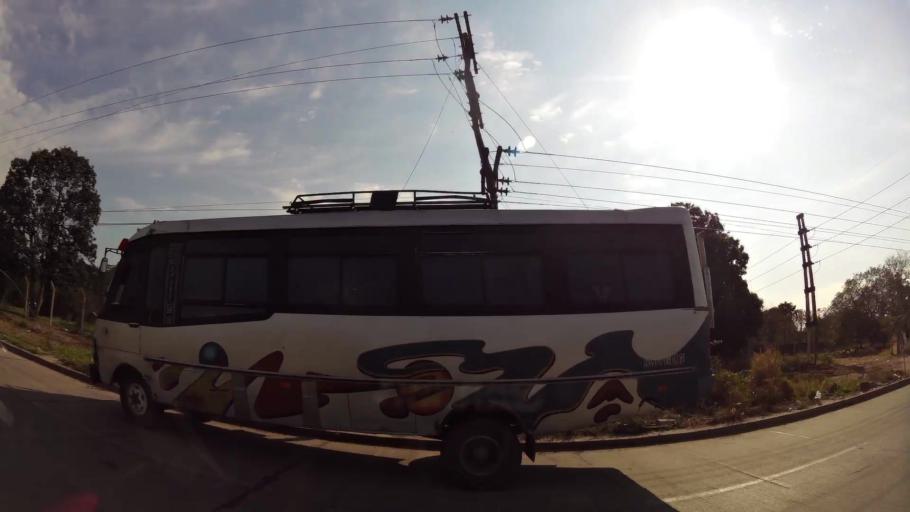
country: BO
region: Santa Cruz
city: Santa Cruz de la Sierra
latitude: -17.7341
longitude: -63.1621
